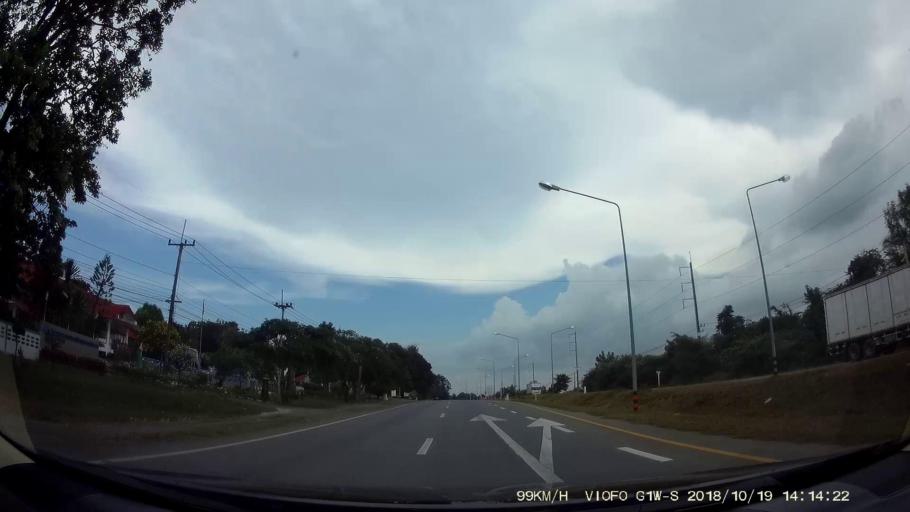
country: TH
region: Chaiyaphum
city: Khon Sawan
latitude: 15.9712
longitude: 102.1875
